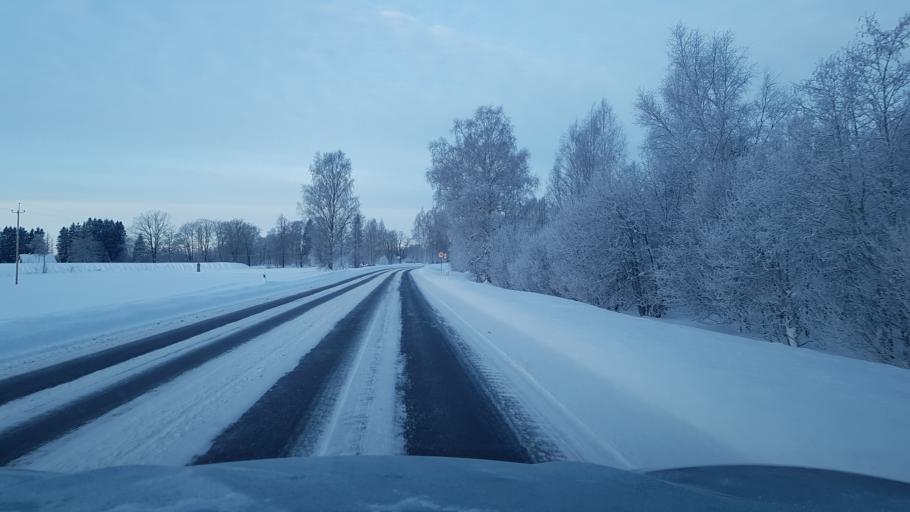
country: EE
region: Ida-Virumaa
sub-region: Johvi vald
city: Johvi
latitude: 59.3454
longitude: 27.4412
